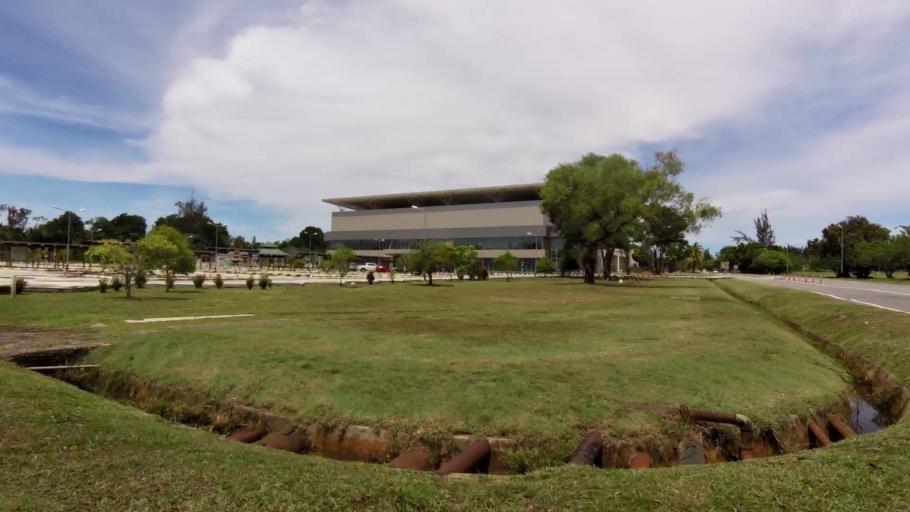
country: BN
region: Belait
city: Seria
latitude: 4.6078
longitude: 114.2947
